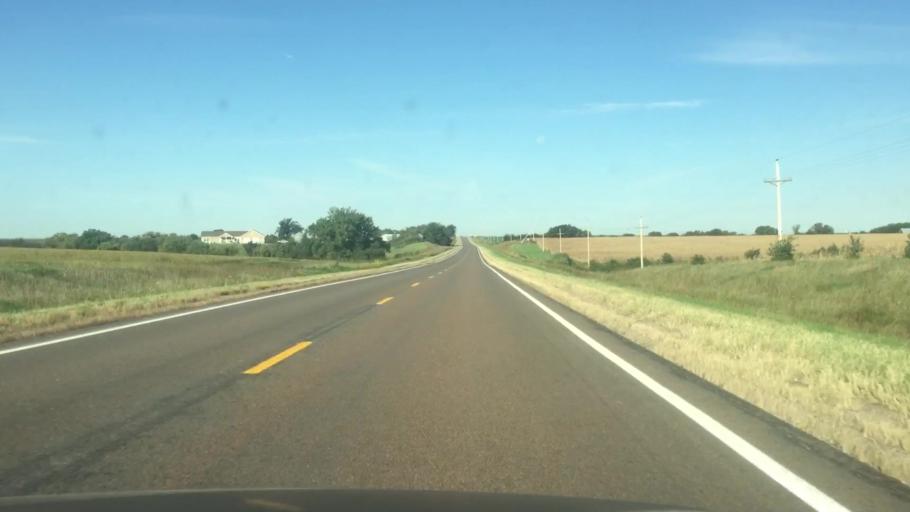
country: US
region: Nebraska
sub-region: Jefferson County
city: Fairbury
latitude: 40.1472
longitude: -97.3532
